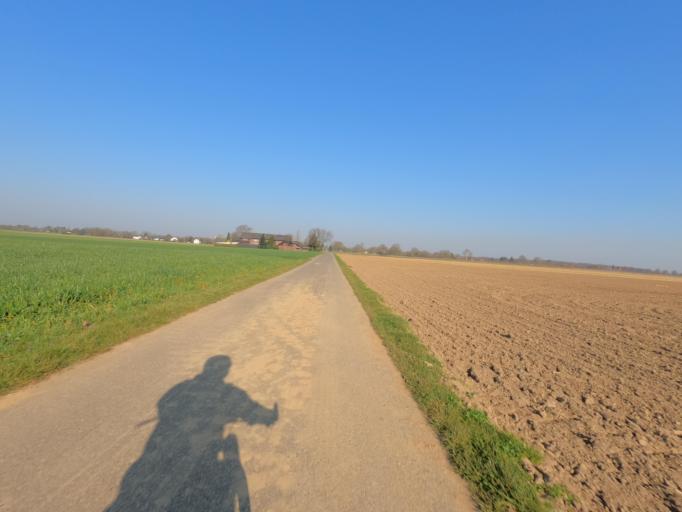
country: DE
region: North Rhine-Westphalia
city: Erkelenz
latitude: 51.0998
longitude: 6.2918
